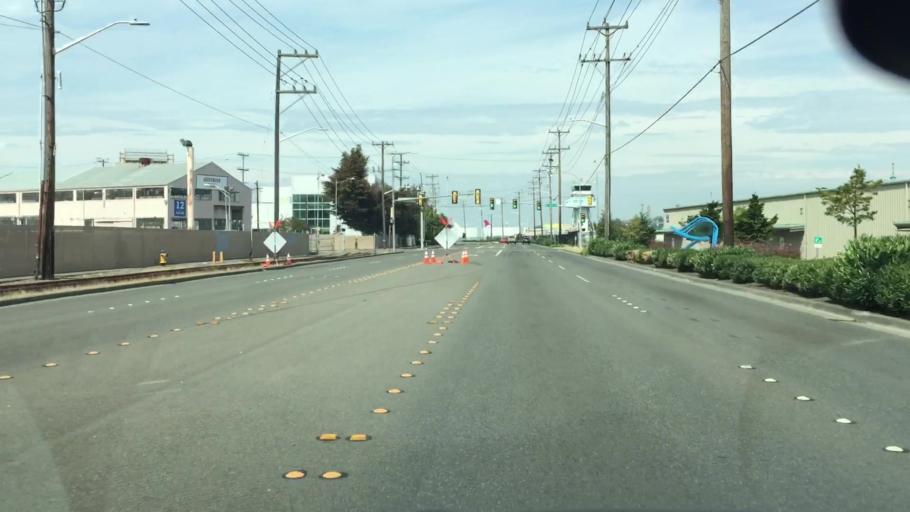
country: US
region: Washington
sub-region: King County
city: Boulevard Park
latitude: 47.5259
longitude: -122.3026
